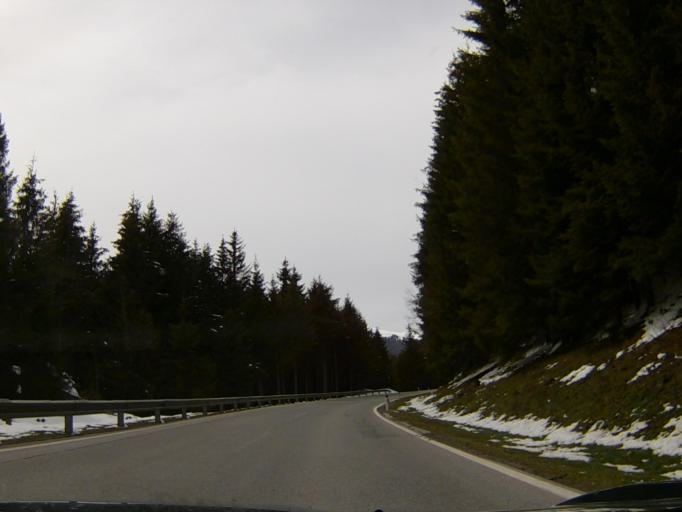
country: AT
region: Tyrol
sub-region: Politischer Bezirk Schwaz
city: Gerlos
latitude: 47.2393
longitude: 12.0745
